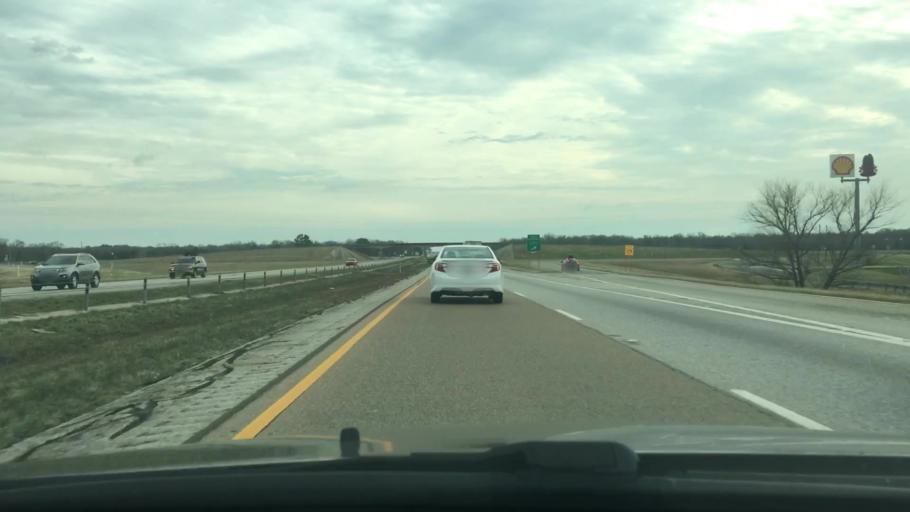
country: US
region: Texas
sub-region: Madison County
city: Madisonville
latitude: 31.0957
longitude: -95.9622
